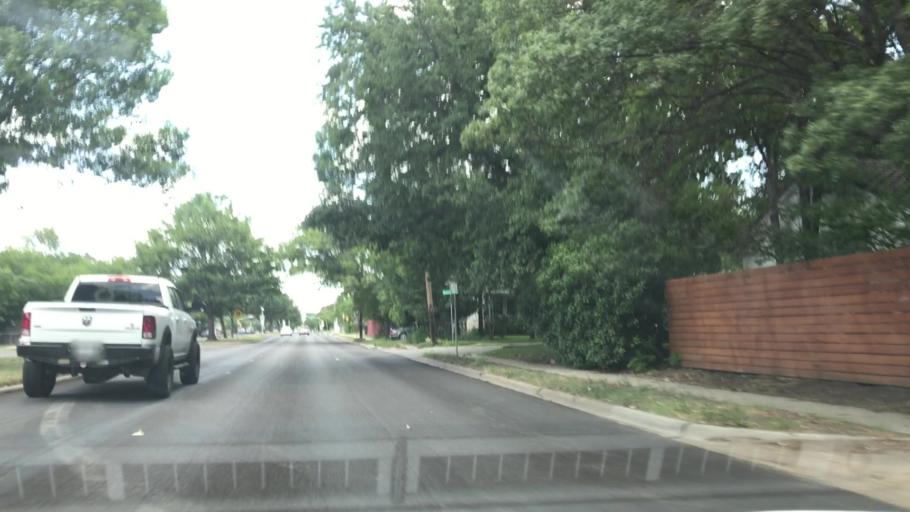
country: US
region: Texas
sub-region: Dallas County
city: University Park
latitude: 32.8678
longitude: -96.8561
